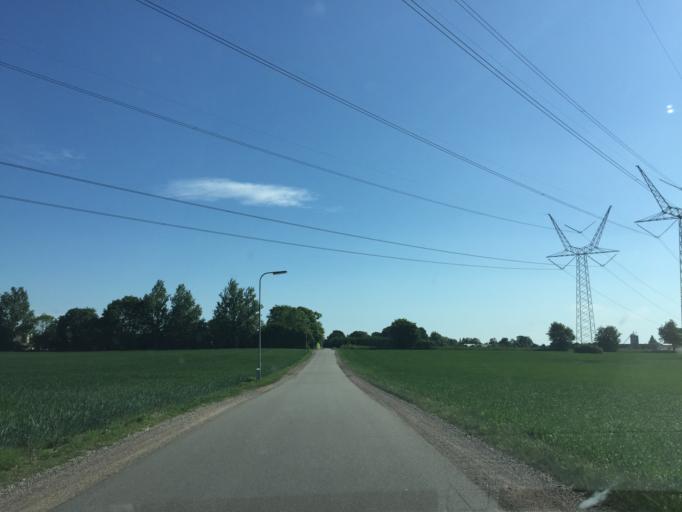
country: DK
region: South Denmark
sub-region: Odense Kommune
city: Hojby
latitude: 55.3375
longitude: 10.3961
